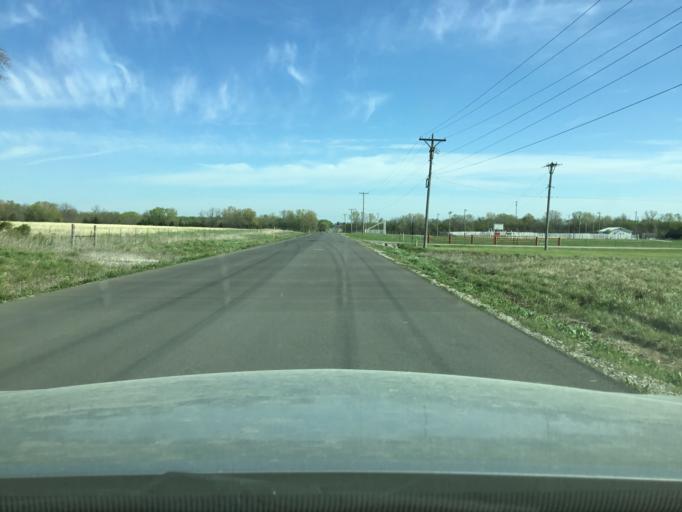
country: US
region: Kansas
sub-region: Neosho County
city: Chanute
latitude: 37.6527
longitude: -95.4435
